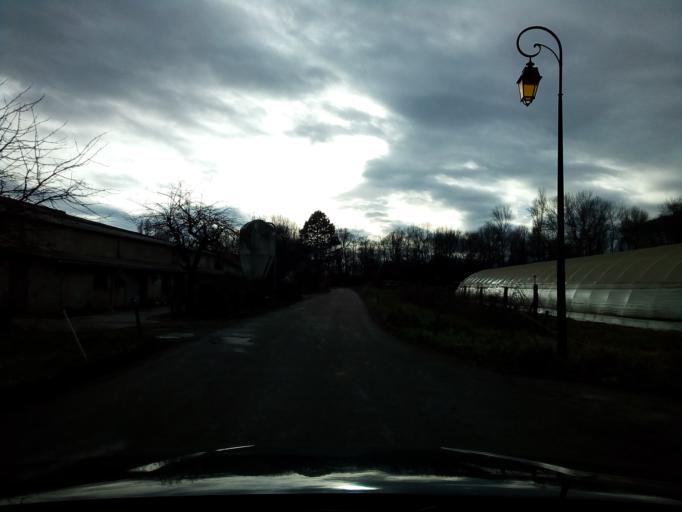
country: FR
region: Rhone-Alpes
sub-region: Departement de l'Isere
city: Crolles
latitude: 45.2812
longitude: 5.8954
